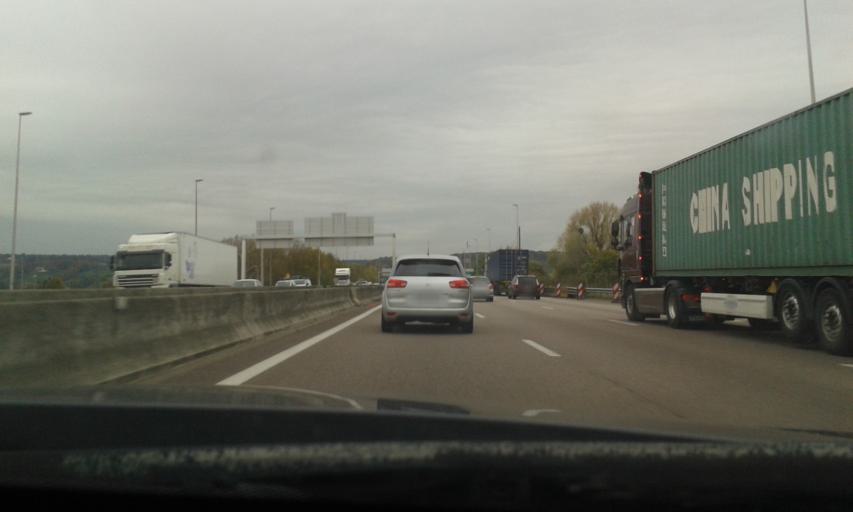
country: FR
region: Haute-Normandie
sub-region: Departement de la Seine-Maritime
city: Oissel
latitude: 49.3291
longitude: 1.0880
